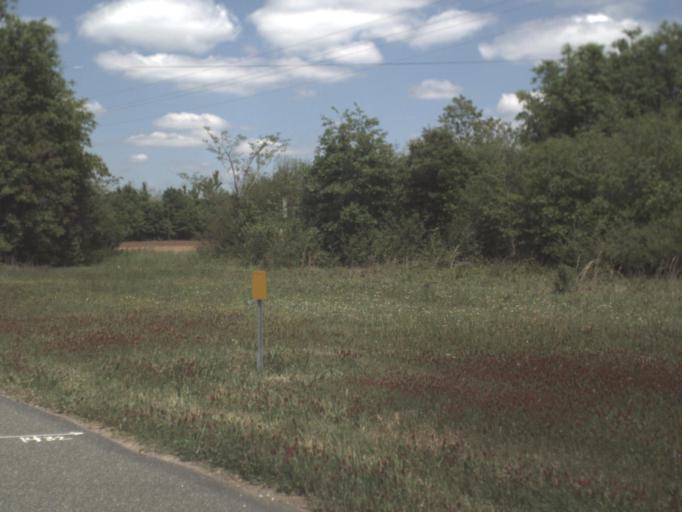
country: US
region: Florida
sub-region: Santa Rosa County
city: Point Baker
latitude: 30.7485
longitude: -87.0426
